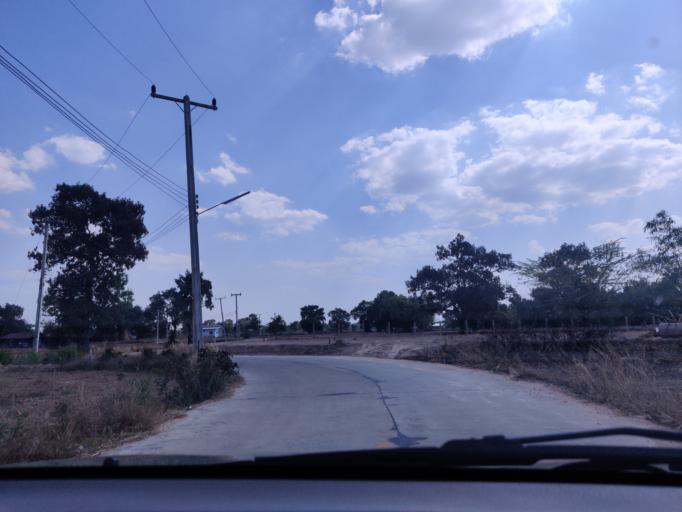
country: TH
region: Sisaket
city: Si Sa Ket
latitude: 15.0886
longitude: 104.3529
